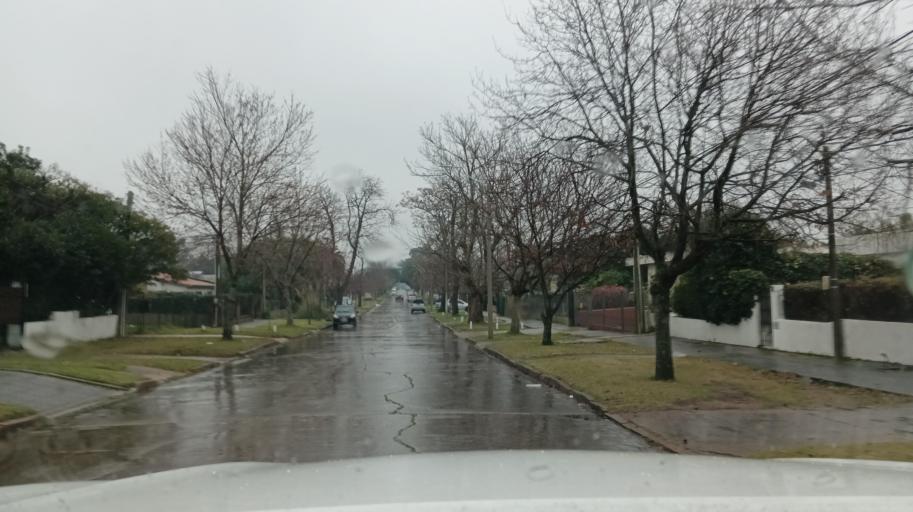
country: UY
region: Canelones
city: Paso de Carrasco
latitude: -34.8775
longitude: -56.0852
